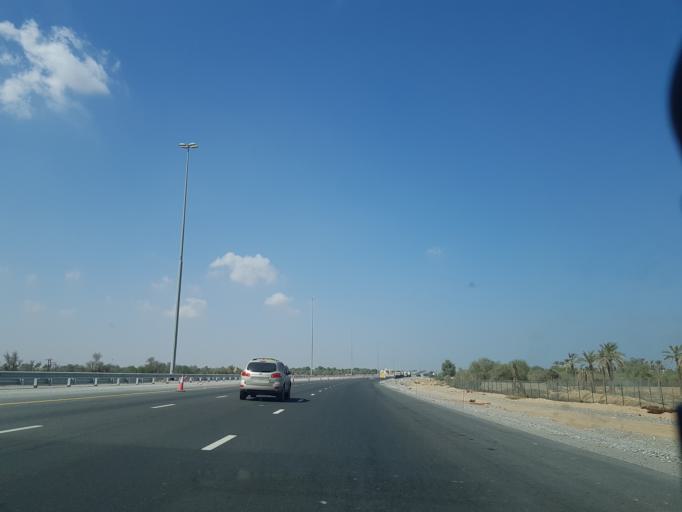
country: AE
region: Ra's al Khaymah
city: Ras al-Khaimah
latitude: 25.6978
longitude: 55.9776
